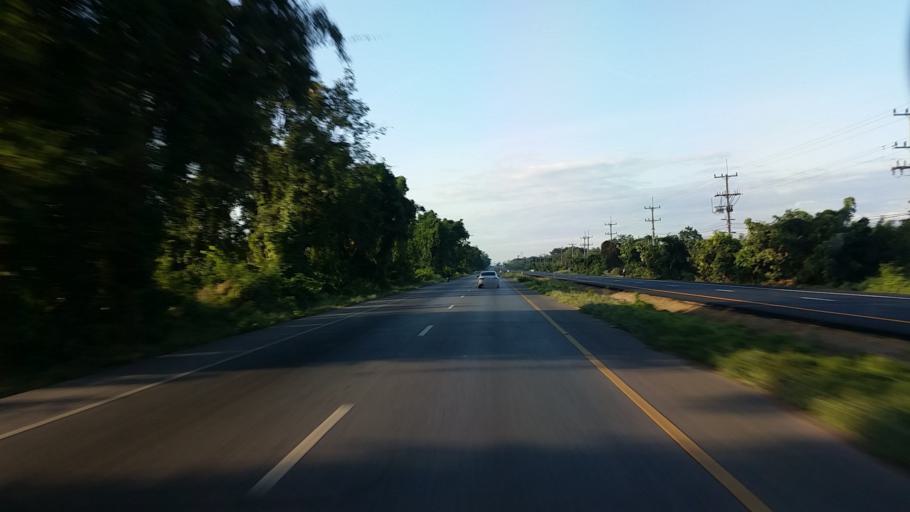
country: TH
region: Lop Buri
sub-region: Amphoe Tha Luang
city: Tha Luang
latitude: 15.1054
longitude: 101.0229
